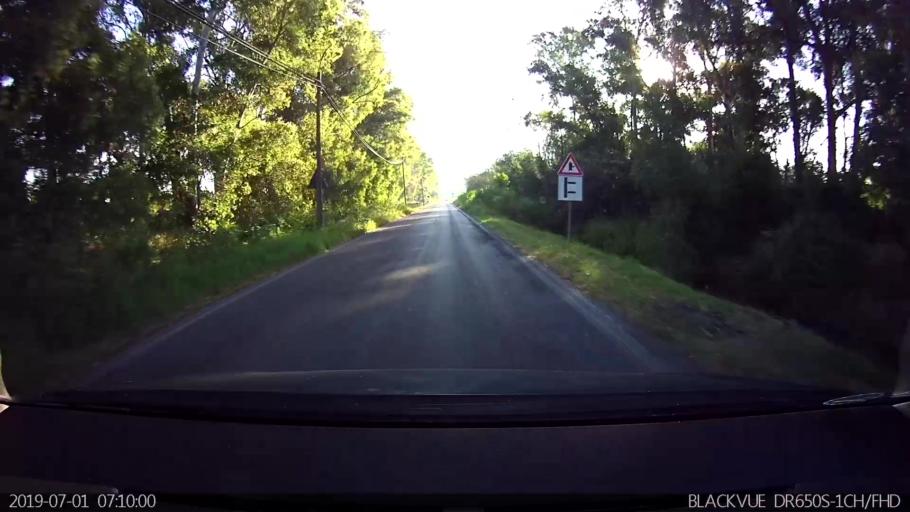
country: IT
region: Latium
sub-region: Provincia di Latina
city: Borgo Hermada
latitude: 41.3088
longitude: 13.1658
